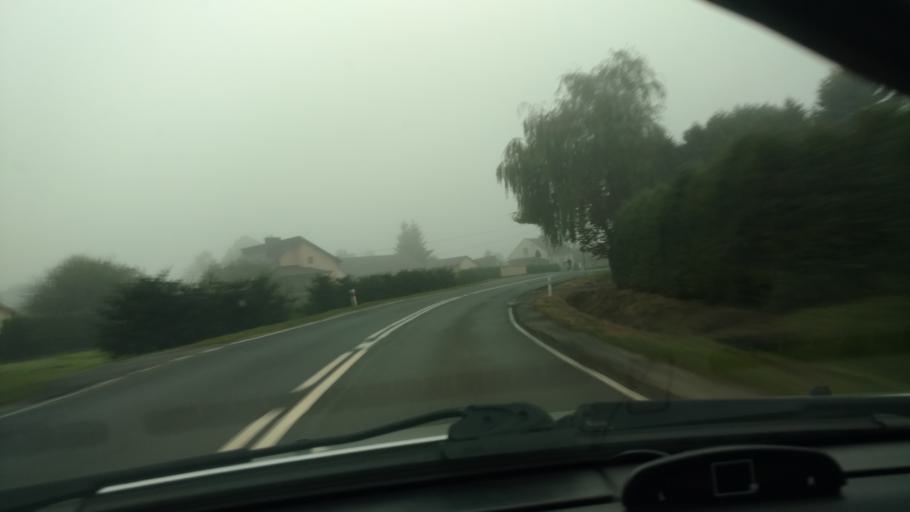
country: PL
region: Subcarpathian Voivodeship
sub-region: Powiat strzyzowski
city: Wisniowa
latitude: 49.8711
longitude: 21.6854
